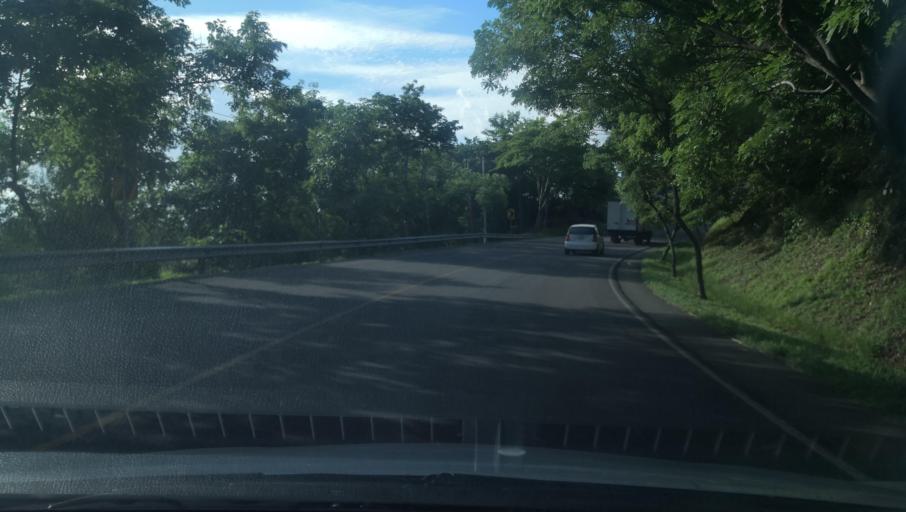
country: NI
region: Madriz
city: Totogalpa
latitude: 13.5588
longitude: -86.4927
